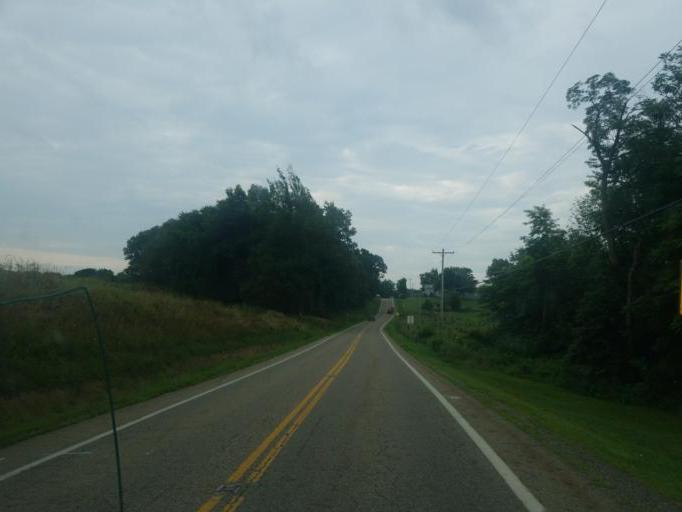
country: US
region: Ohio
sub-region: Carroll County
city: Lake Mohawk
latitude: 40.6369
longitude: -81.2180
